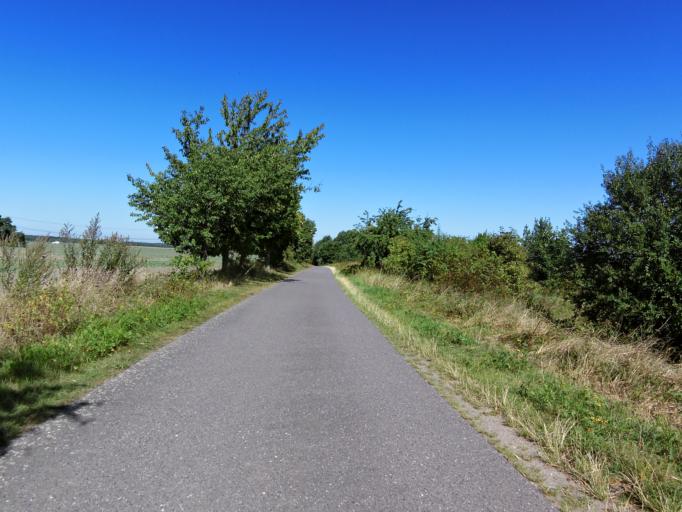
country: DE
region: Saxony
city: Dommitzsch
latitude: 51.6571
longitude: 12.8467
